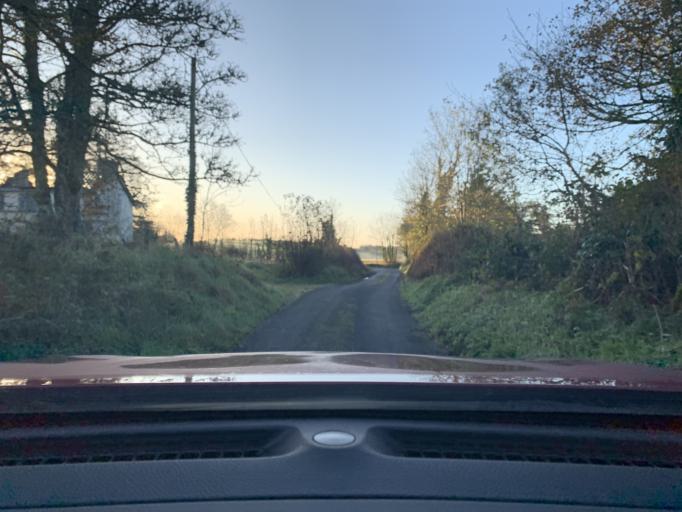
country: IE
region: Connaught
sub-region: Sligo
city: Ballymote
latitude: 54.0608
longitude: -8.5183
